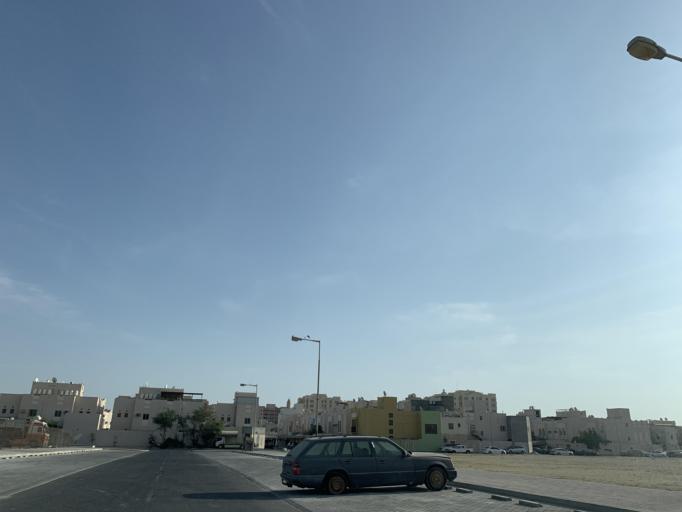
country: BH
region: Central Governorate
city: Madinat Hamad
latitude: 26.1252
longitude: 50.4871
